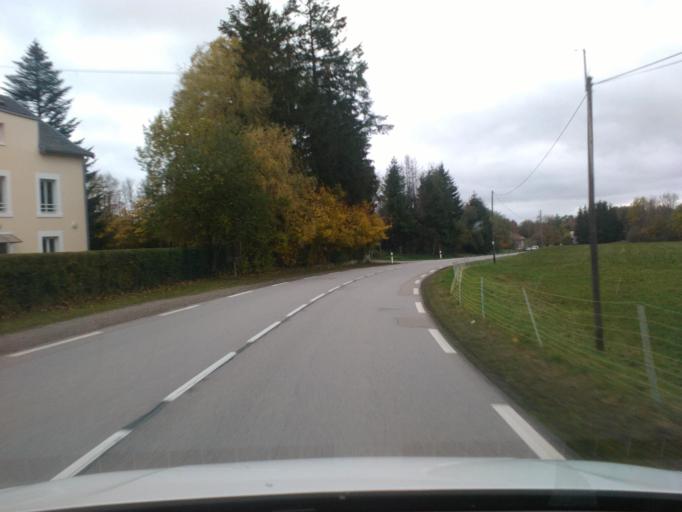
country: FR
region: Lorraine
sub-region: Departement des Vosges
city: Ban-de-Laveline
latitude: 48.3428
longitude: 7.1078
